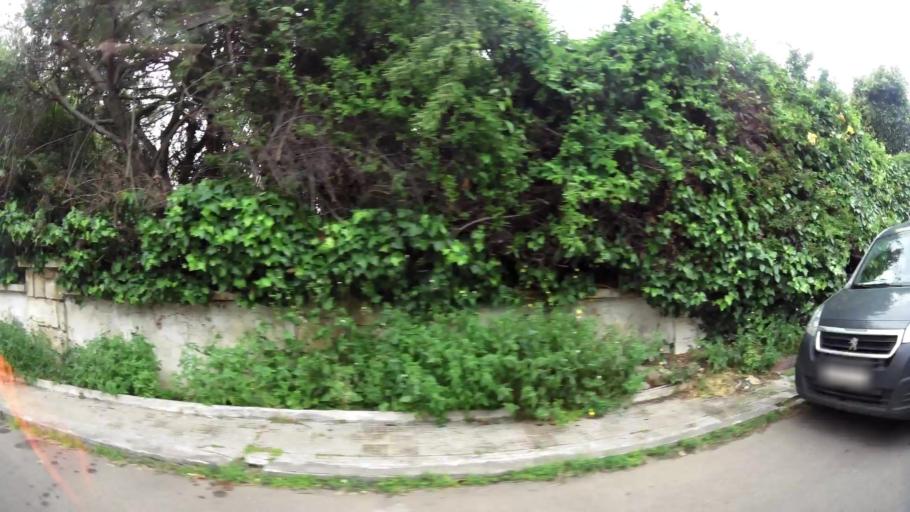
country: MA
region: Grand Casablanca
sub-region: Casablanca
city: Casablanca
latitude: 33.5608
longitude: -7.6316
